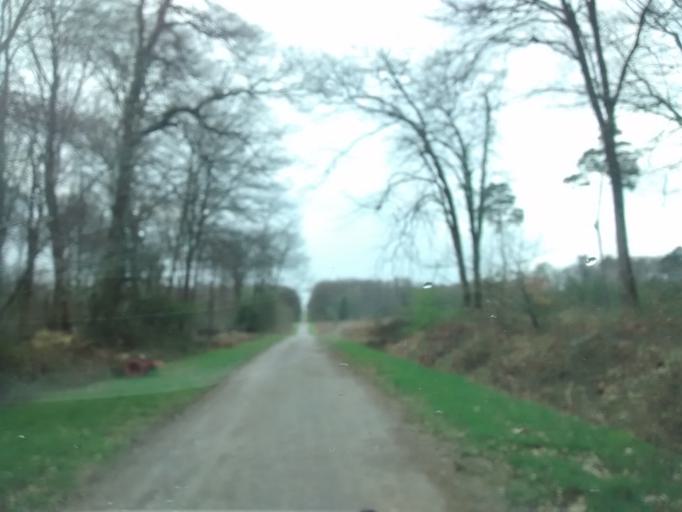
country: FR
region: Brittany
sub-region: Departement d'Ille-et-Vilaine
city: Fouillard
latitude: 48.1717
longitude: -1.5465
